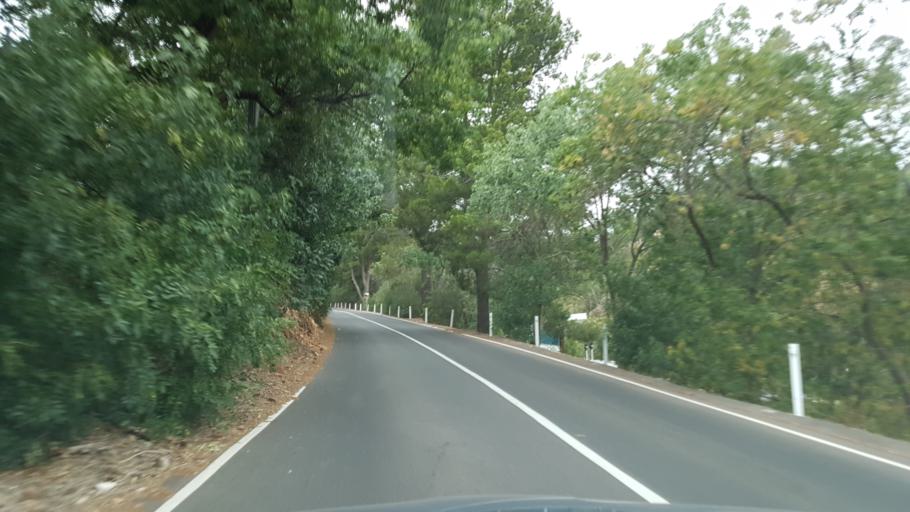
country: AU
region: South Australia
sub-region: Burnside
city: Mount Osmond
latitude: -34.9631
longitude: 138.6487
